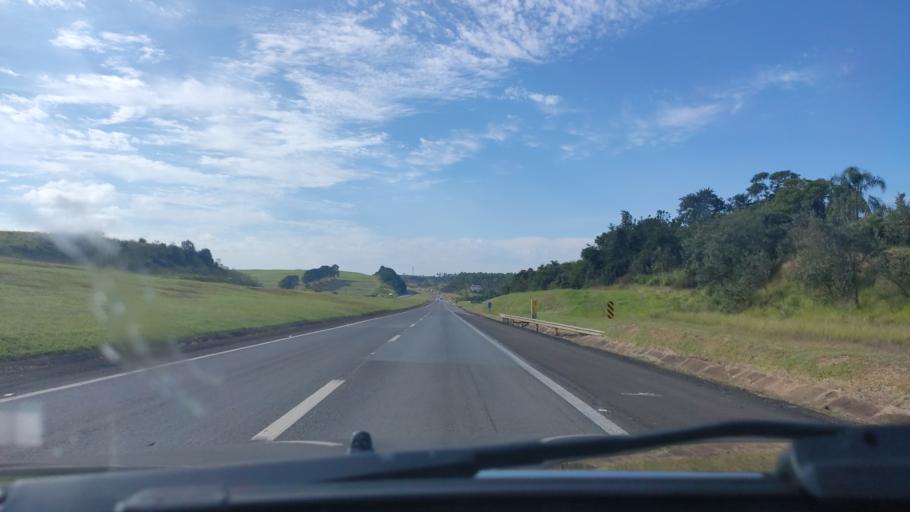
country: BR
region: Sao Paulo
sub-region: Itatinga
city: Itatinga
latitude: -23.1284
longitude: -48.4731
